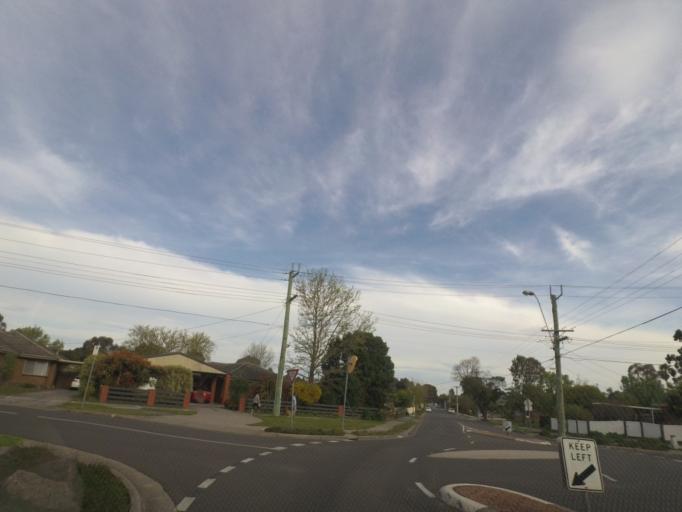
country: AU
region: Victoria
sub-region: Knox
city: Scoresby
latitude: -37.8939
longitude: 145.2405
